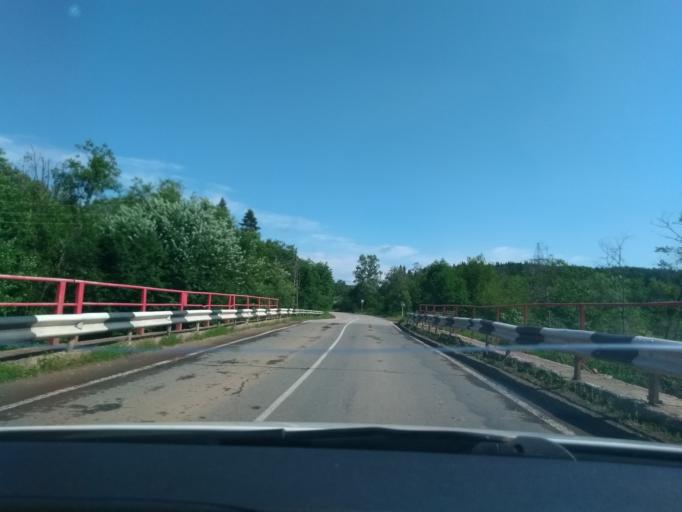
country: RU
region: Perm
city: Bershet'
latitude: 57.8187
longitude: 56.5044
